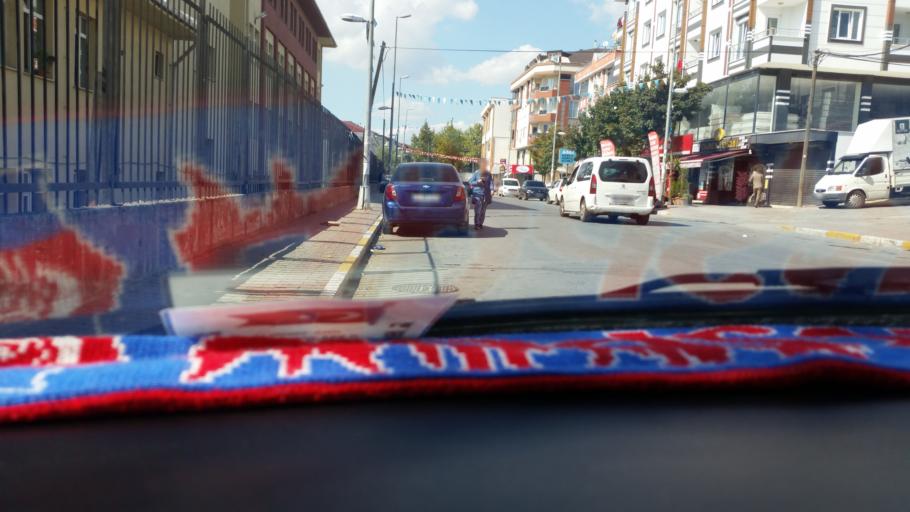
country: TR
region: Istanbul
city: Esenyurt
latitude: 41.0760
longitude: 28.6331
